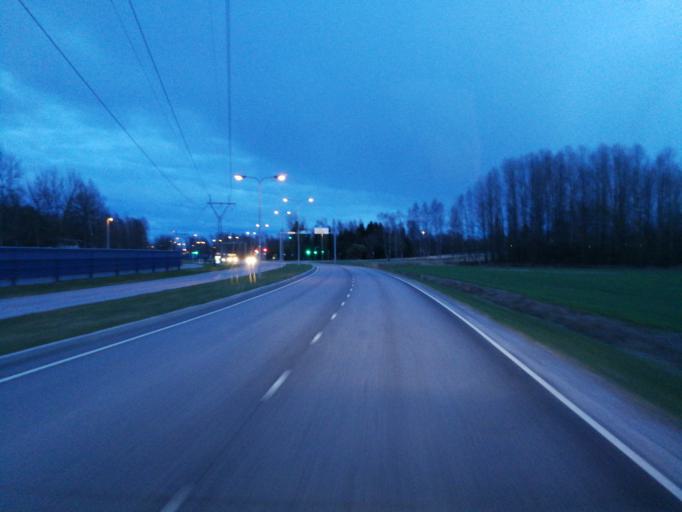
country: FI
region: Varsinais-Suomi
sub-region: Turku
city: Raisio
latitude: 60.4559
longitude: 22.1942
